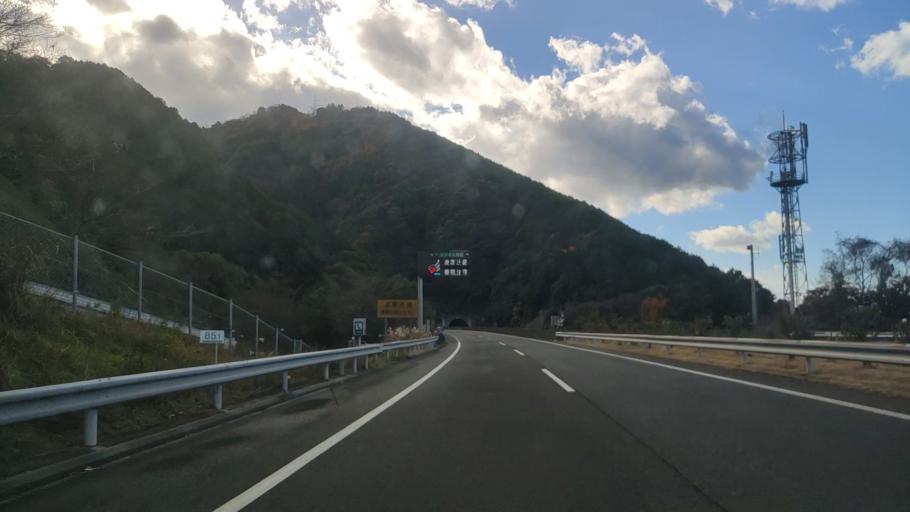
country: JP
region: Ehime
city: Niihama
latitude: 33.9237
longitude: 133.3195
